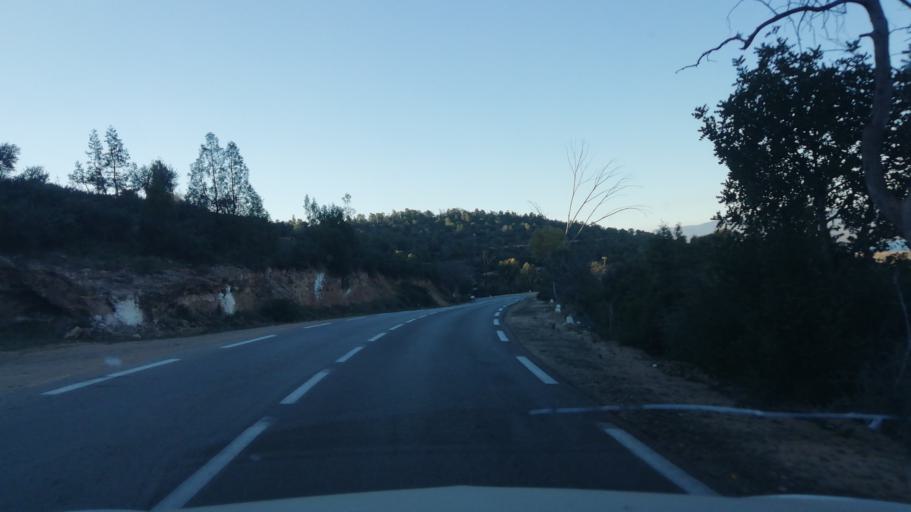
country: DZ
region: Tlemcen
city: Beni Mester
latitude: 34.8169
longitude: -1.6345
